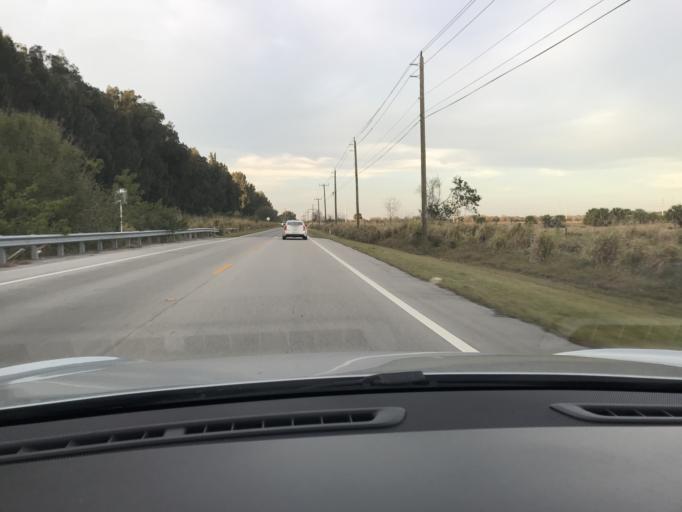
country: US
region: Florida
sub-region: Saint Lucie County
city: Lakewood Park
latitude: 27.5264
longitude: -80.4312
